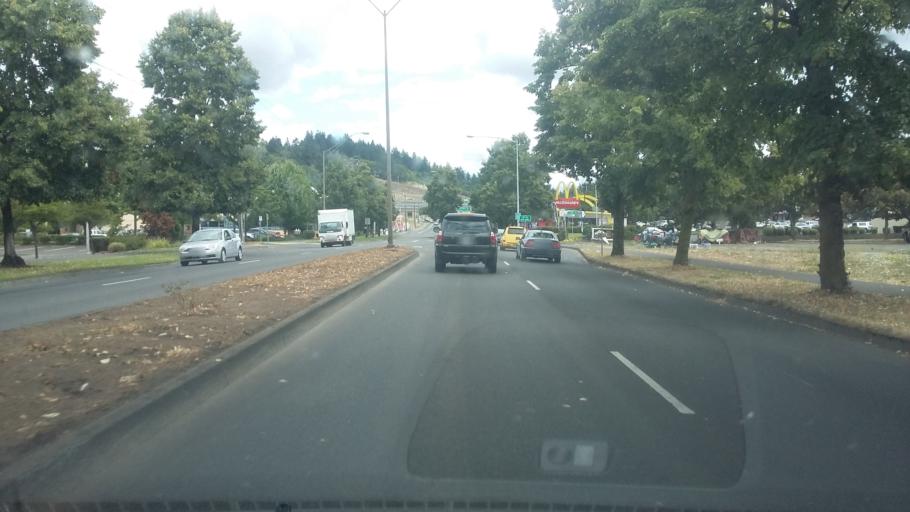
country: US
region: Oregon
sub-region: Multnomah County
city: Lents
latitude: 45.4974
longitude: -122.5718
